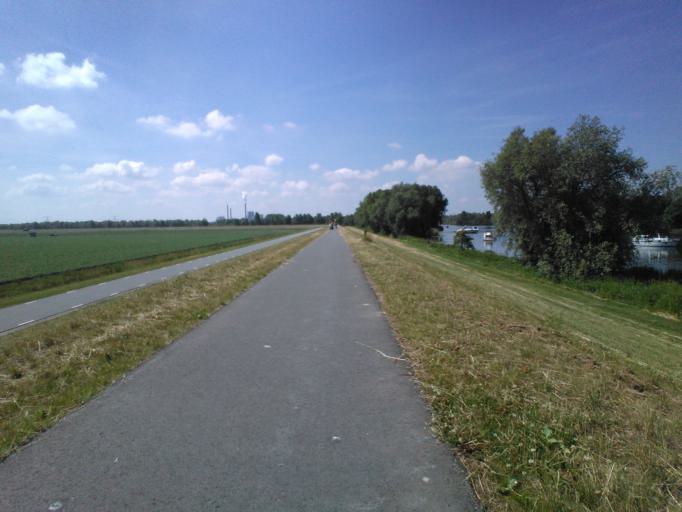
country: NL
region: North Brabant
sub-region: Gemeente Geertruidenberg
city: Geertruidenberg
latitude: 51.7430
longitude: 4.8558
